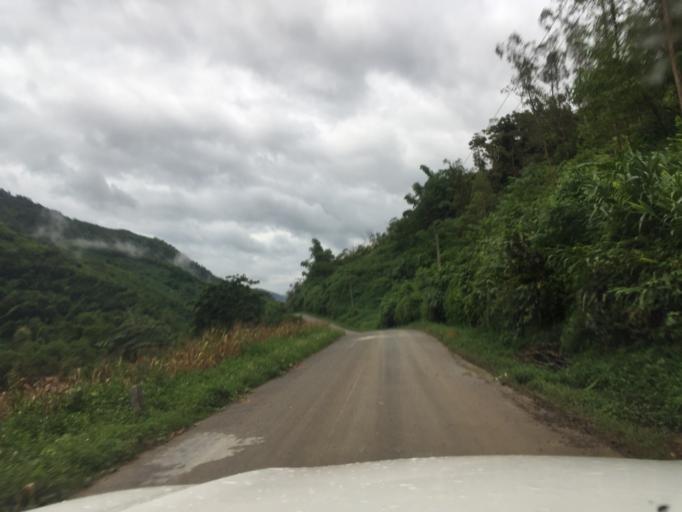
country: LA
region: Oudomxai
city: Muang La
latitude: 21.0001
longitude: 102.2326
